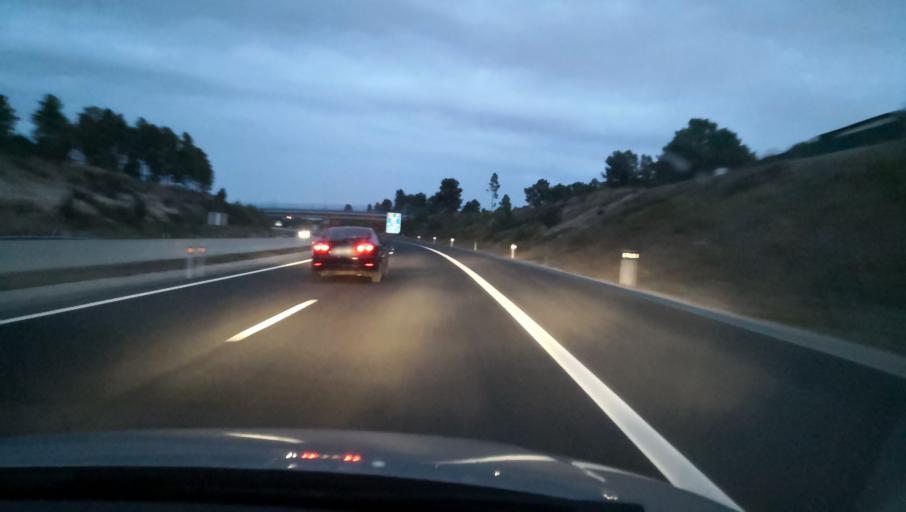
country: PT
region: Setubal
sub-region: Seixal
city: Aldeia de Paio Pires
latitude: 38.5838
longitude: -9.0775
